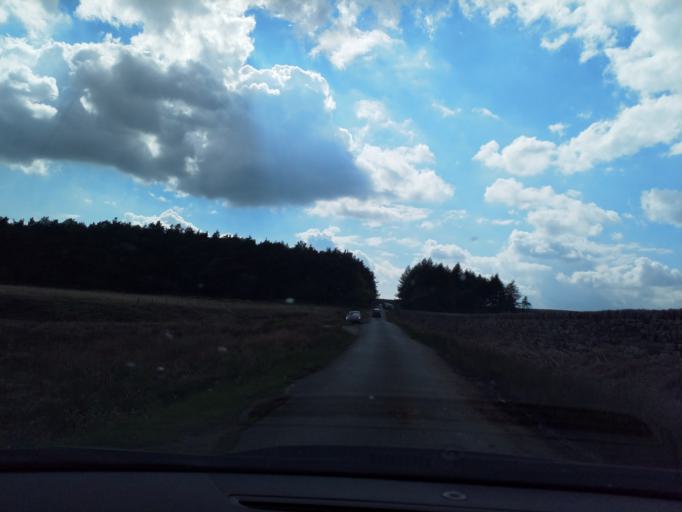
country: GB
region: England
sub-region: Derbyshire
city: Hathersage
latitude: 53.3556
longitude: -1.6552
